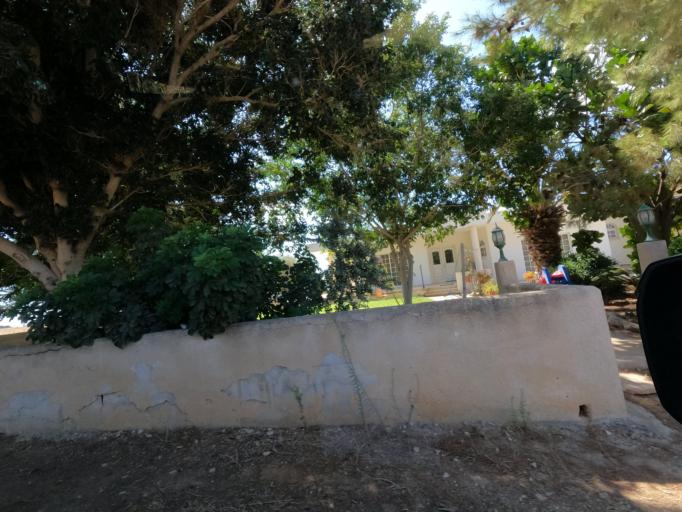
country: CY
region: Pafos
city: Paphos
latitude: 34.7407
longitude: 32.4988
